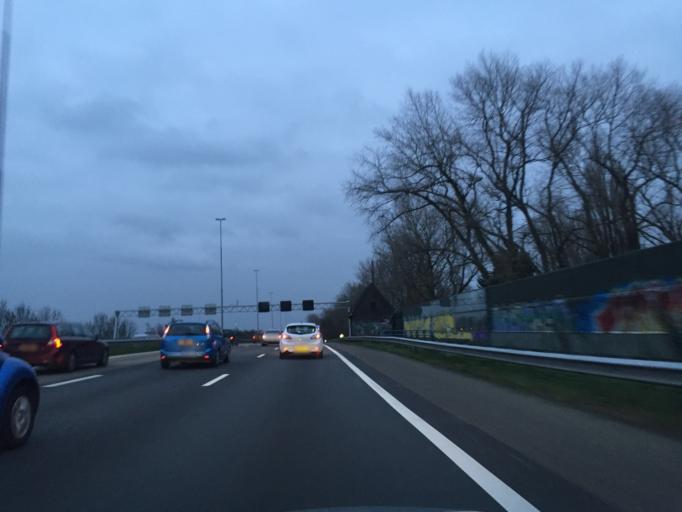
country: NL
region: South Holland
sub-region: Gemeente Schiedam
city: Schiedam
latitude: 51.9668
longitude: 4.4031
